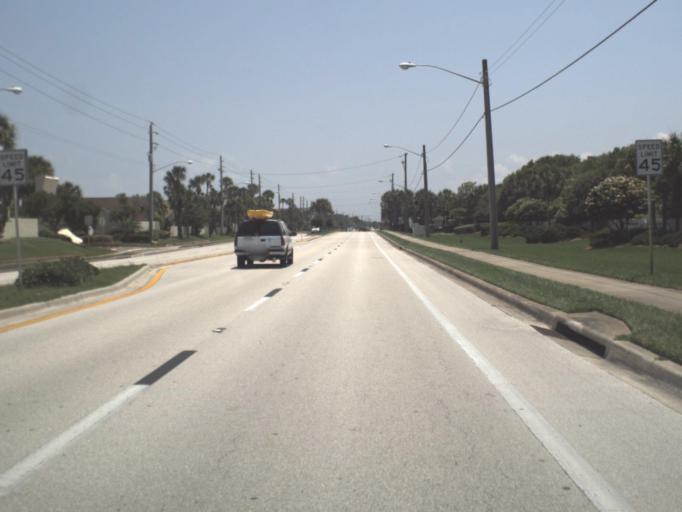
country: US
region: Florida
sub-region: Saint Johns County
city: Butler Beach
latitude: 29.8127
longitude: -81.2678
